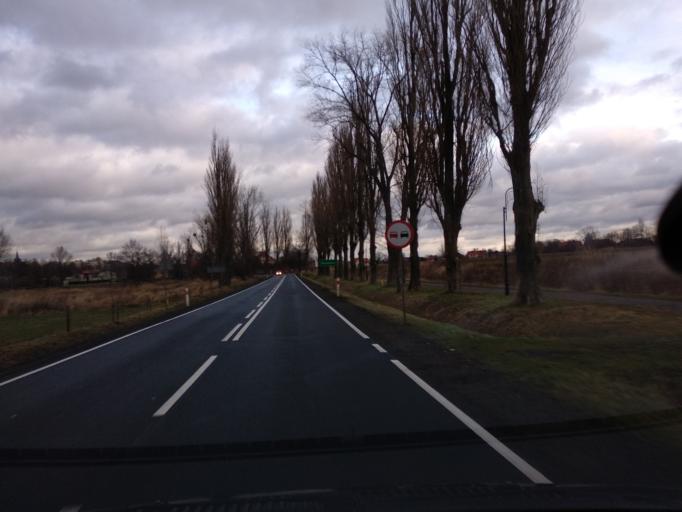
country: PL
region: Lower Silesian Voivodeship
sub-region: Powiat olesnicki
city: Miedzyborz
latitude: 51.3913
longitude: 17.6617
